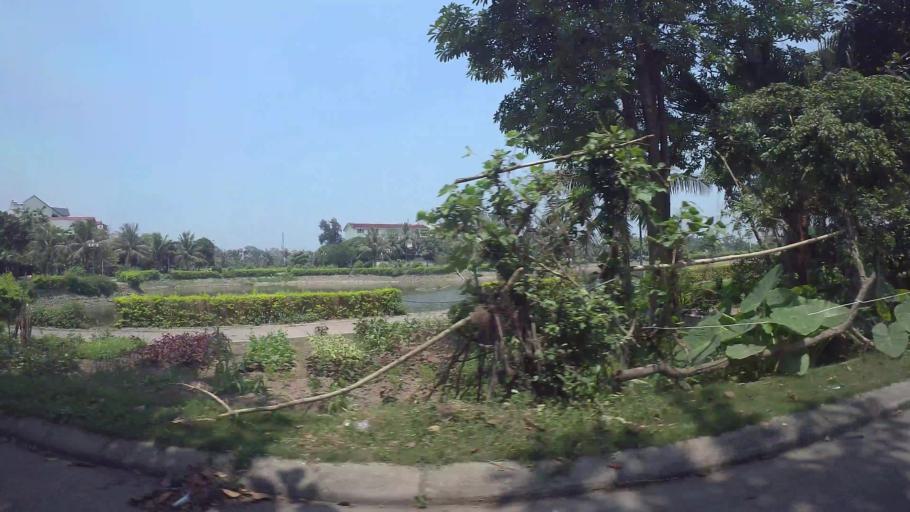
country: VN
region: Ha Noi
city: Trau Quy
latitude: 21.0282
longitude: 105.9100
